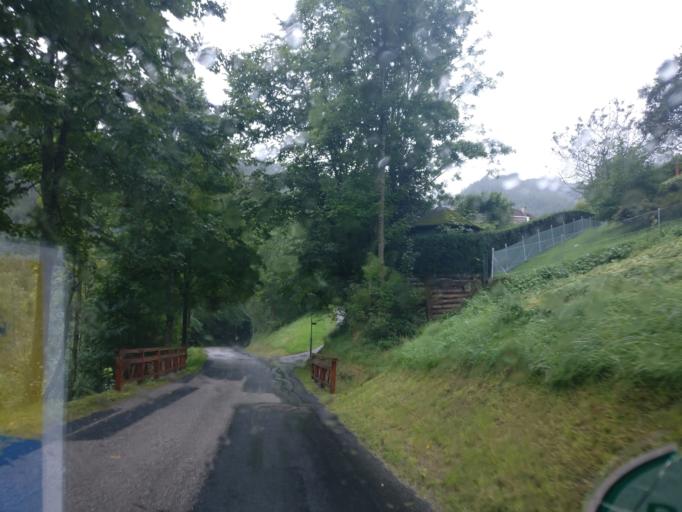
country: AT
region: Lower Austria
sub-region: Politischer Bezirk Neunkirchen
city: Semmering
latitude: 47.6590
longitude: 15.8231
